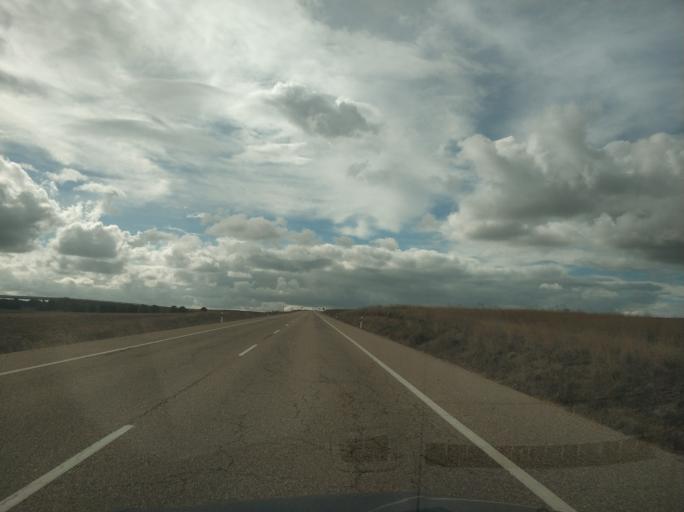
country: ES
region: Castille and Leon
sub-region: Provincia de Valladolid
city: Pollos
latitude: 41.4396
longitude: -5.0959
